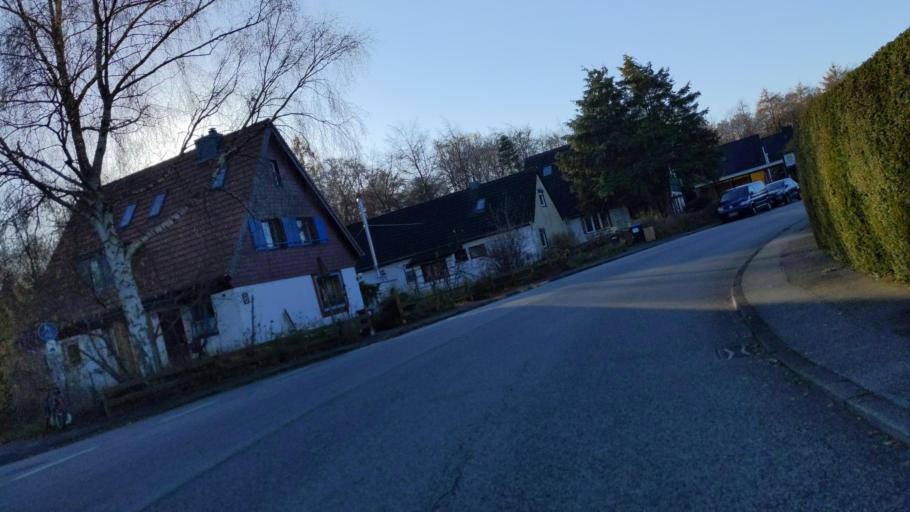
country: DE
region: Schleswig-Holstein
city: Ratekau
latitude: 53.8989
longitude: 10.7484
